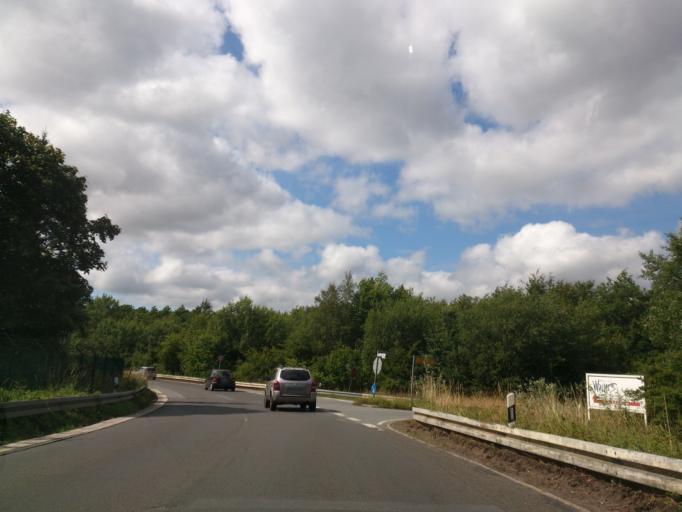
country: DE
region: Schleswig-Holstein
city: Flensburg
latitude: 54.8168
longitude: 9.4218
